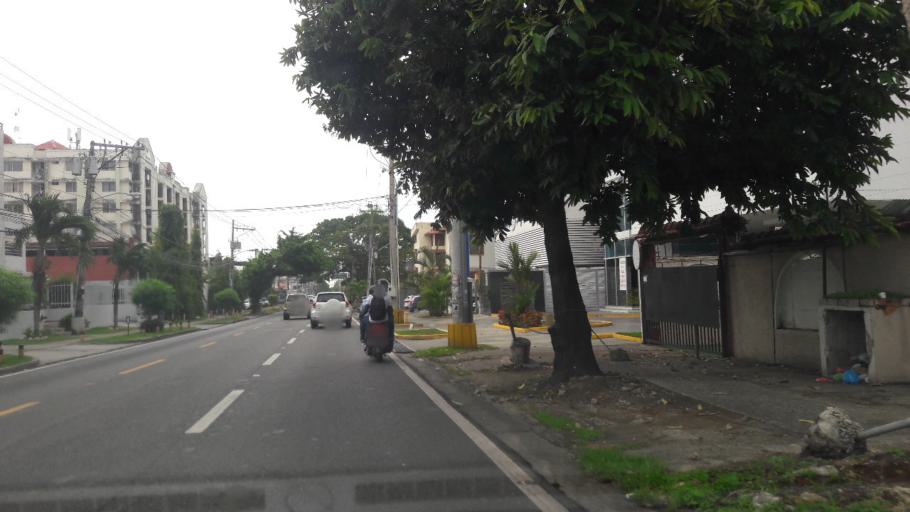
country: PA
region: Panama
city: Panama
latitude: 9.0063
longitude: -79.5002
